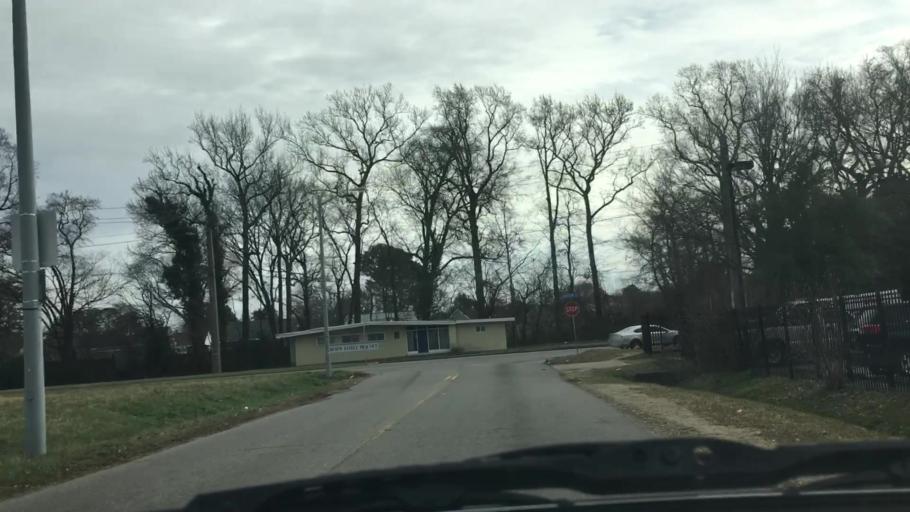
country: US
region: Virginia
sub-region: City of Norfolk
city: Norfolk
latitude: 36.8932
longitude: -76.2272
